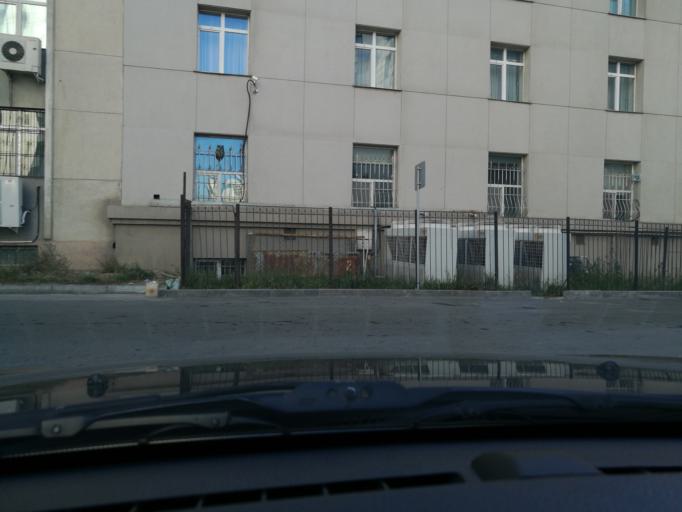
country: MN
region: Ulaanbaatar
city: Ulaanbaatar
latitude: 47.9192
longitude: 106.9218
